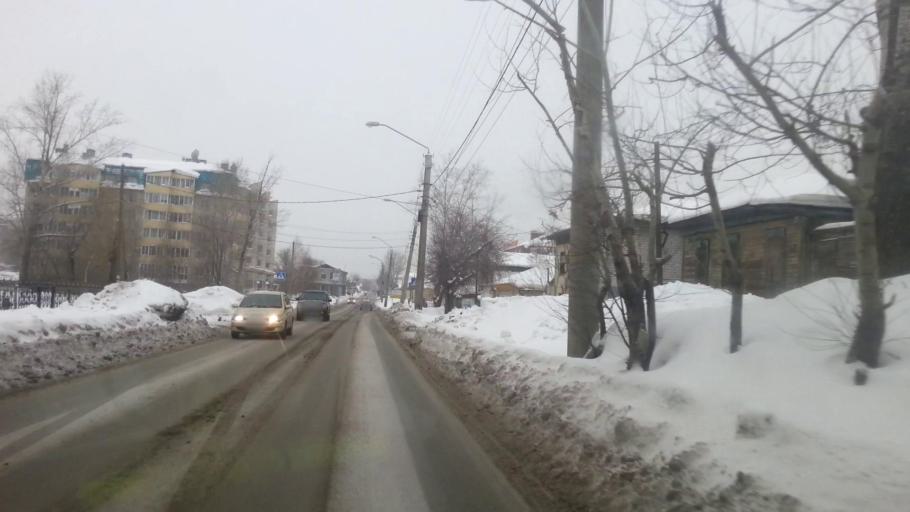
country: RU
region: Altai Krai
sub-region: Gorod Barnaulskiy
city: Barnaul
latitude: 53.3313
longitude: 83.7637
